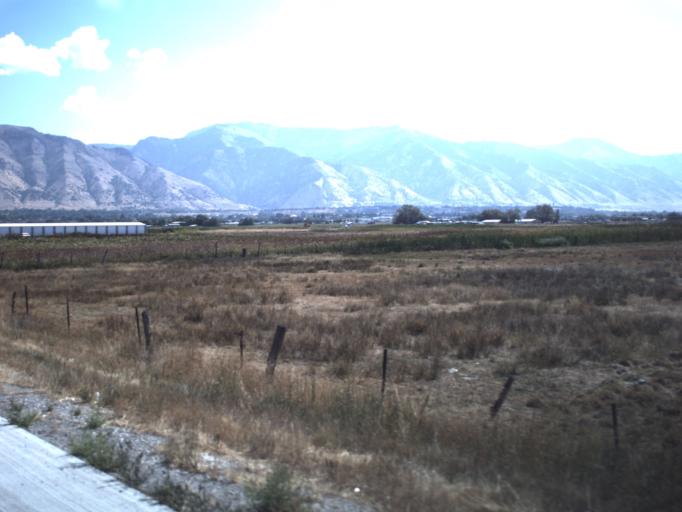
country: US
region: Utah
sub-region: Cache County
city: Hyde Park
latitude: 41.7779
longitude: -111.8544
